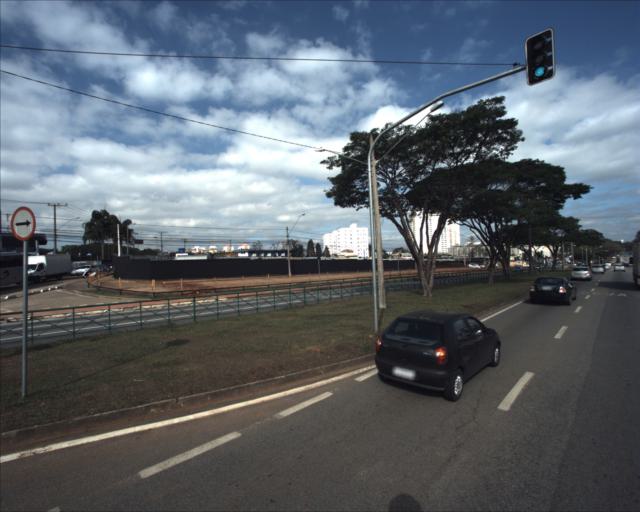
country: BR
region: Sao Paulo
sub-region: Sorocaba
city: Sorocaba
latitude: -23.5268
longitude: -47.4903
